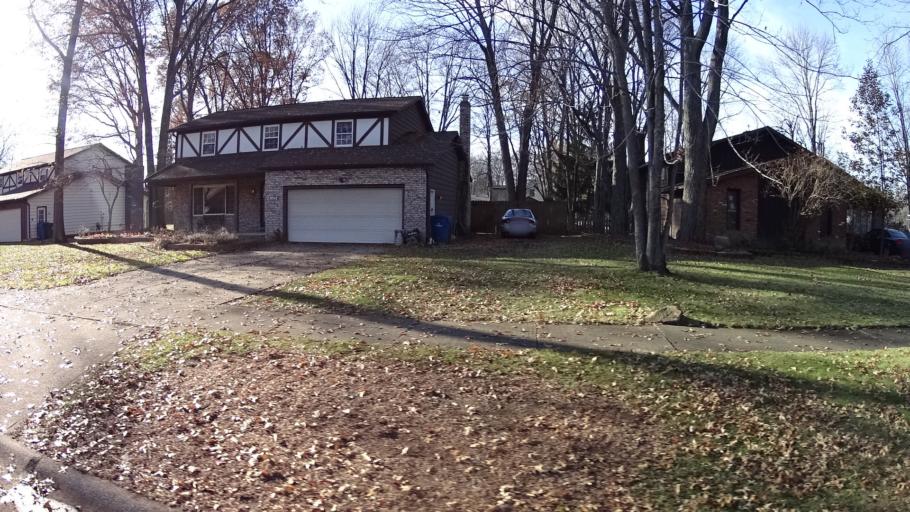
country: US
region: Ohio
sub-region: Lorain County
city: North Ridgeville
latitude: 41.3910
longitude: -81.9893
